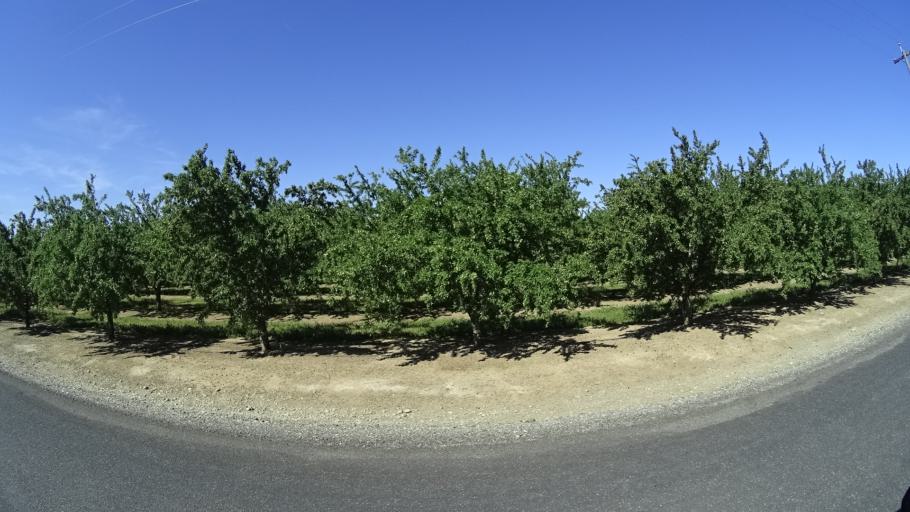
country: US
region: California
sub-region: Glenn County
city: Hamilton City
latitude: 39.6624
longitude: -122.1035
